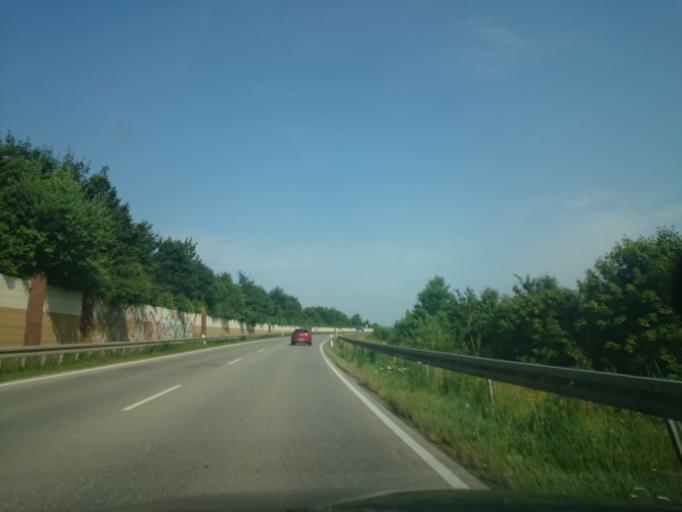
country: DE
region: Bavaria
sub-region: Swabia
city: Merching
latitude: 48.2554
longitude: 10.9824
